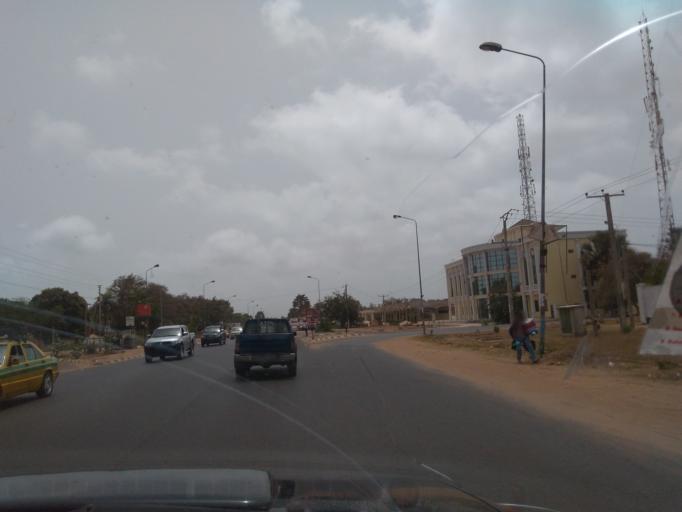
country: GM
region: Banjul
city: Bakau
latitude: 13.4522
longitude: -16.7139
